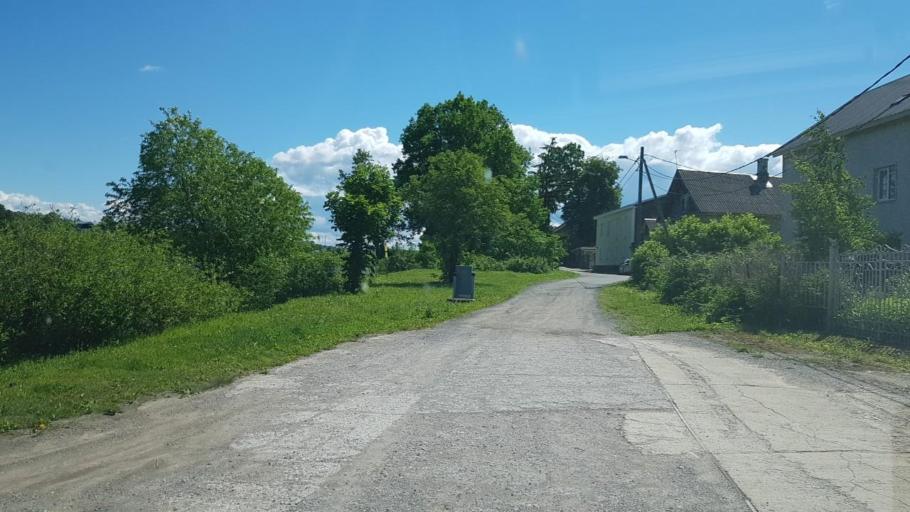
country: EE
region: Ida-Virumaa
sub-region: Narva linn
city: Narva
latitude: 59.3923
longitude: 28.1969
